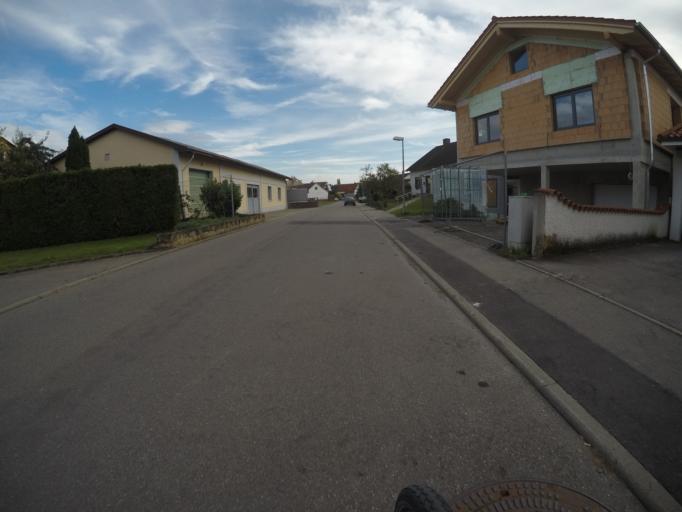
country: DE
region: Baden-Wuerttemberg
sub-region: Regierungsbezirk Stuttgart
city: Herrenberg
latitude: 48.5608
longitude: 8.9059
